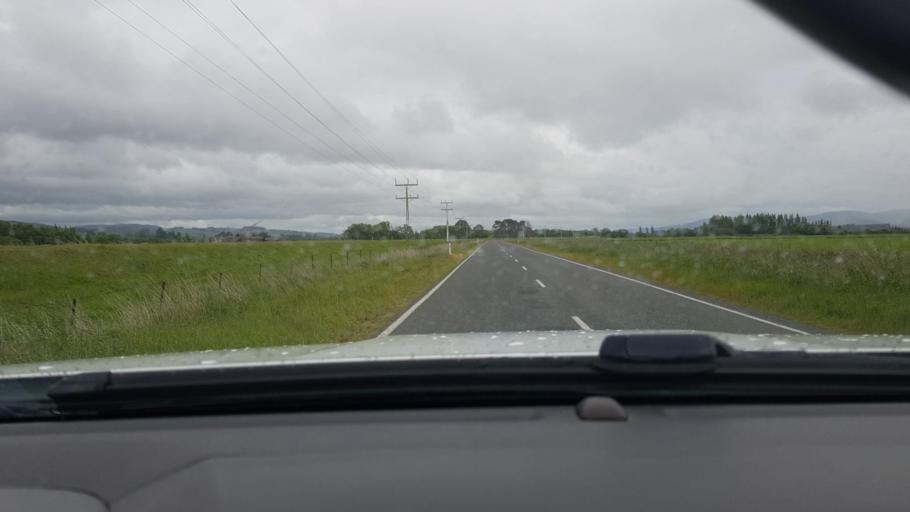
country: NZ
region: Southland
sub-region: Southland District
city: Winton
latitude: -45.8360
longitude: 168.3712
